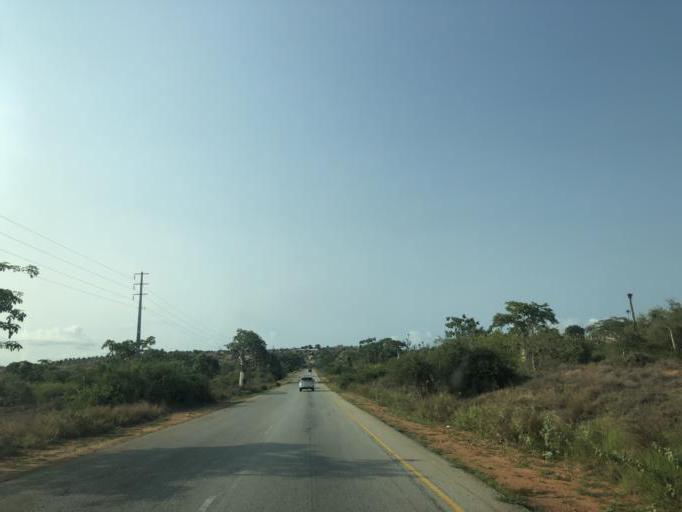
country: AO
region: Luanda
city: Luanda
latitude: -9.2933
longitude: 13.1341
